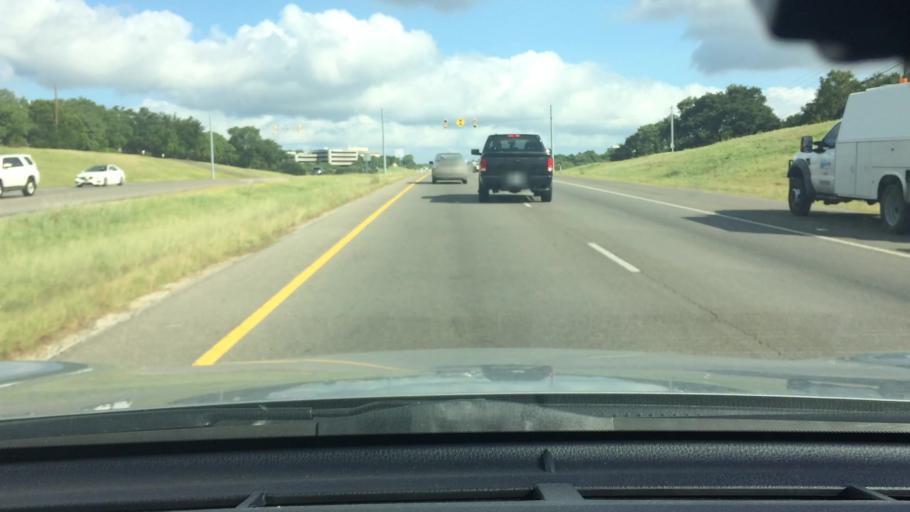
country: US
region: Texas
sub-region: Travis County
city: West Lake Hills
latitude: 30.2789
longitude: -97.8204
